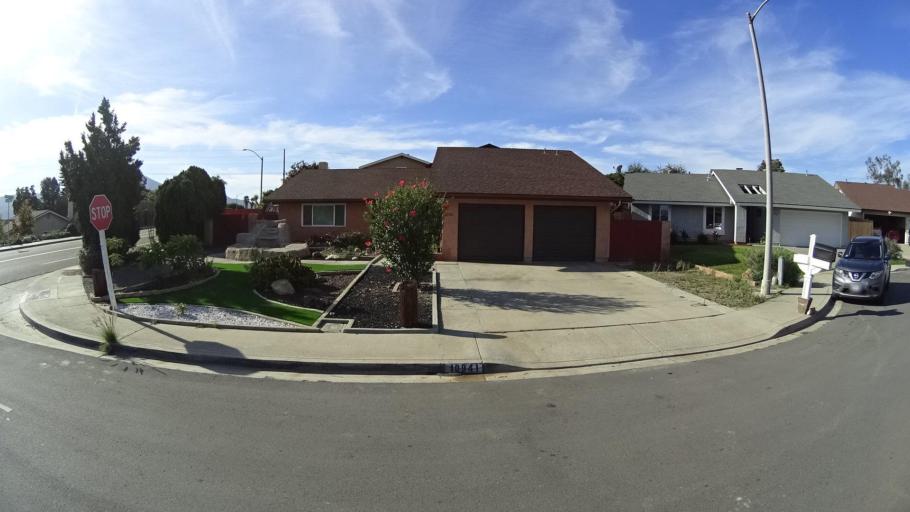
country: US
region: California
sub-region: San Diego County
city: Casa de Oro-Mount Helix
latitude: 32.7416
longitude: -116.9612
